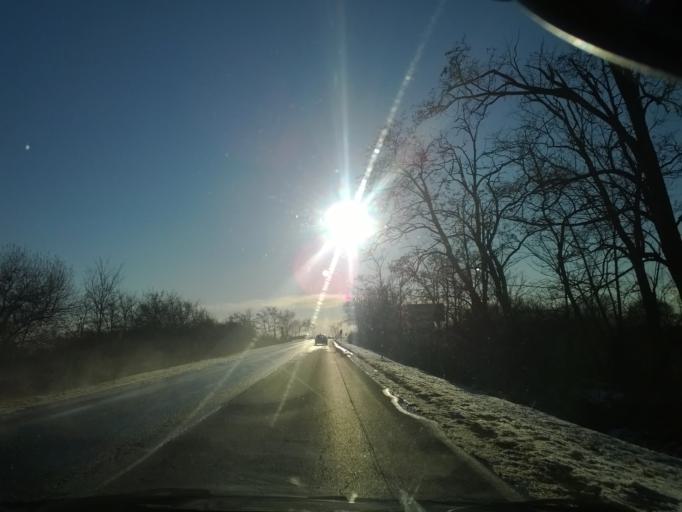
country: HU
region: Fejer
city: Enying
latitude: 46.9513
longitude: 18.1814
